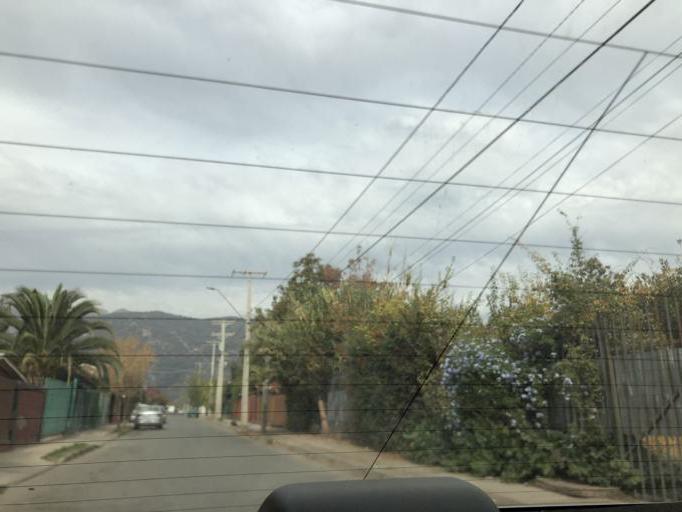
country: CL
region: Santiago Metropolitan
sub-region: Provincia de Cordillera
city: Puente Alto
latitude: -33.6068
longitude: -70.5228
